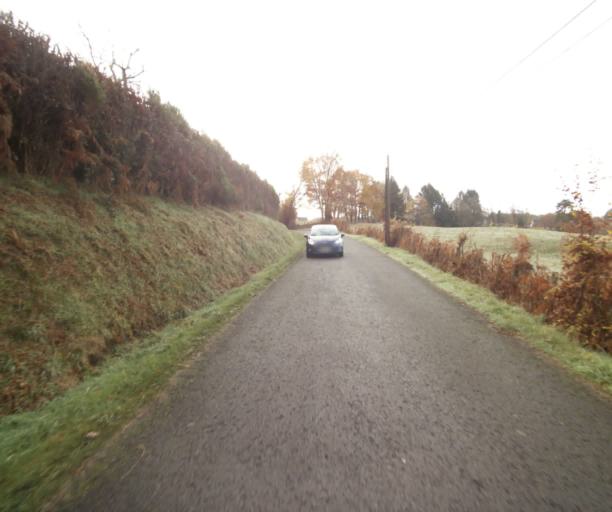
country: FR
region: Limousin
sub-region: Departement de la Correze
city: Cornil
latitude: 45.2073
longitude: 1.7095
